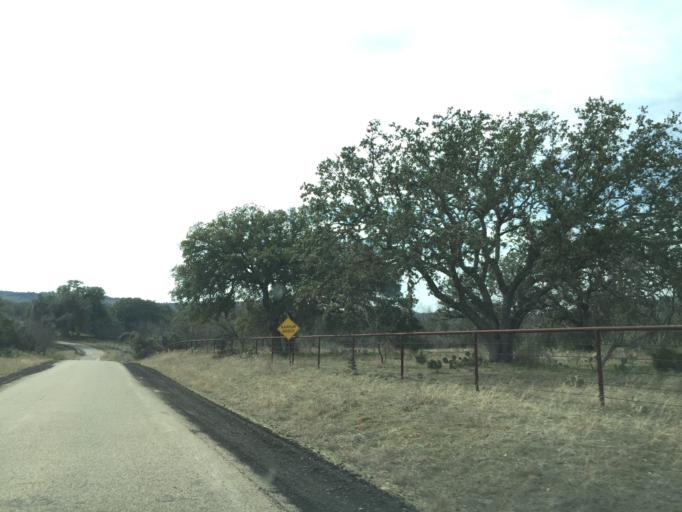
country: US
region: Texas
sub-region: Gillespie County
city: Fredericksburg
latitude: 30.4524
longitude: -98.6507
